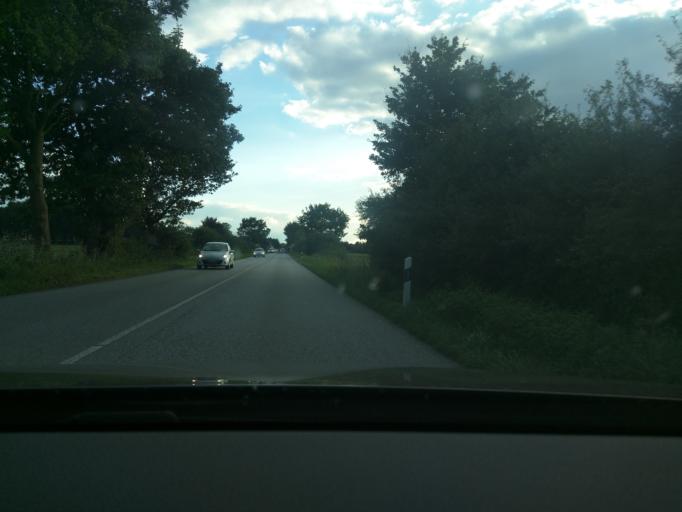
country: DE
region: Schleswig-Holstein
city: Lutau
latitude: 53.4407
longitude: 10.5574
